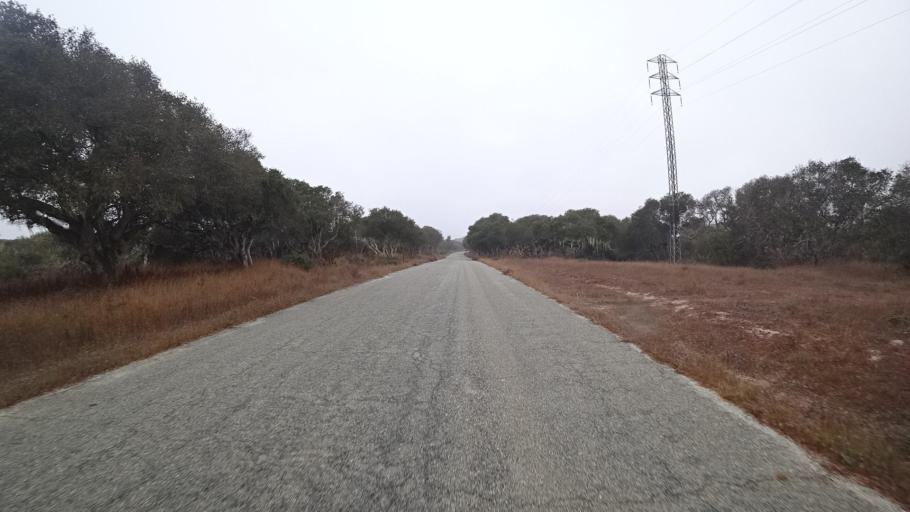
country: US
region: California
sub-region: Monterey County
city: Marina
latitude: 36.6436
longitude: -121.7785
